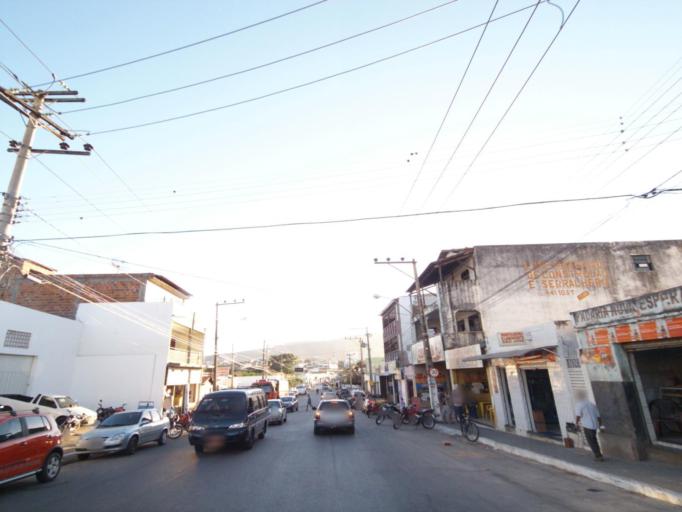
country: BR
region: Bahia
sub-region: Brumado
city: Brumado
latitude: -14.2034
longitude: -41.6596
